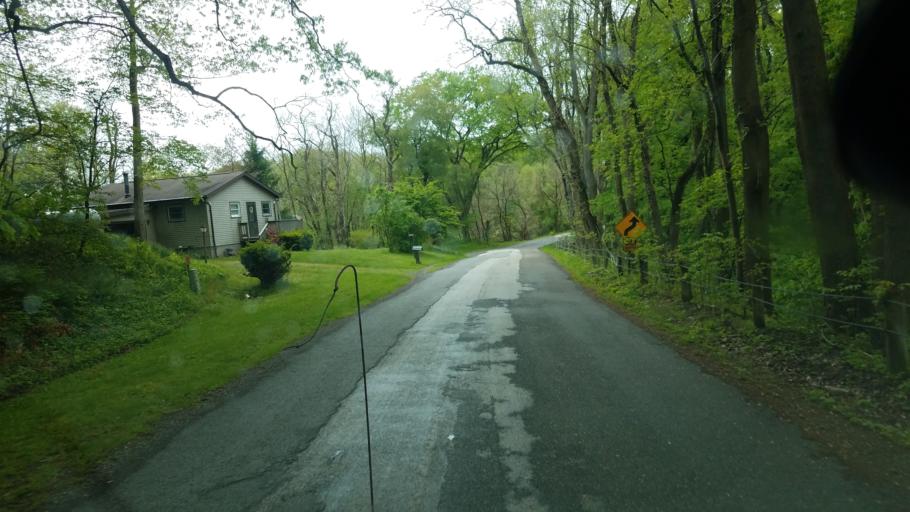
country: US
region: Ohio
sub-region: Tuscarawas County
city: Rockford
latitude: 40.3877
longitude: -81.1506
